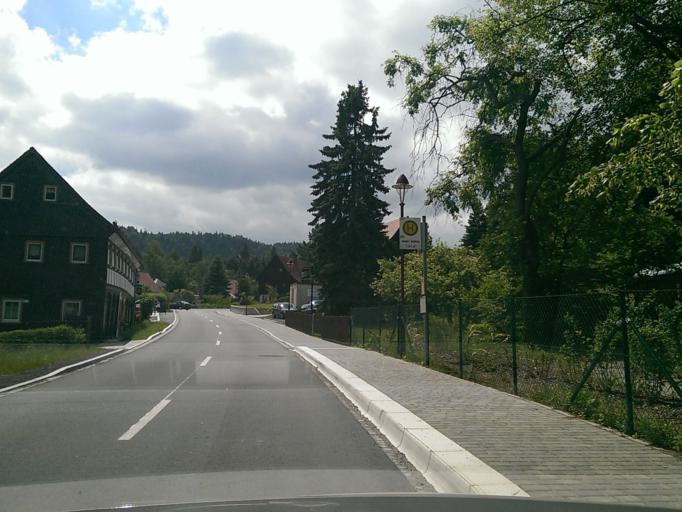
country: DE
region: Saxony
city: Kurort Jonsdorf
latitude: 50.8581
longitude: 14.6936
